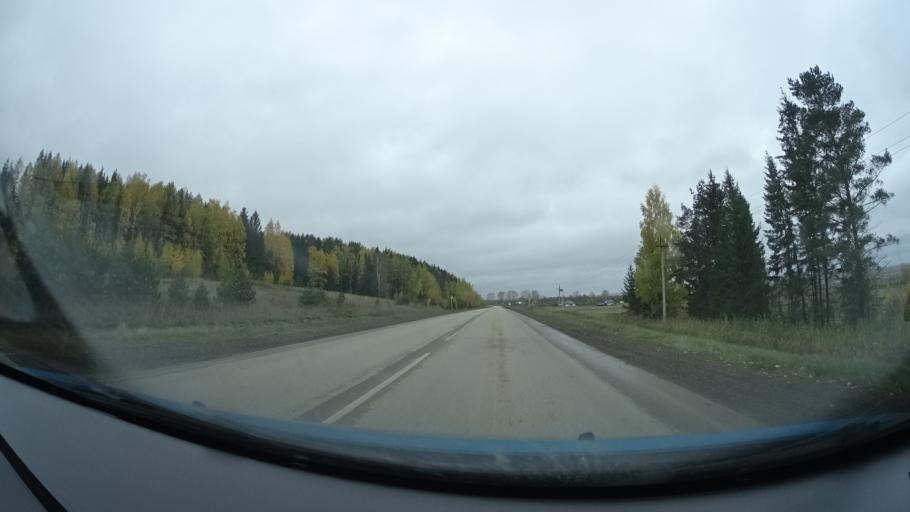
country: RU
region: Perm
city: Osa
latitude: 57.2103
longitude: 55.5899
